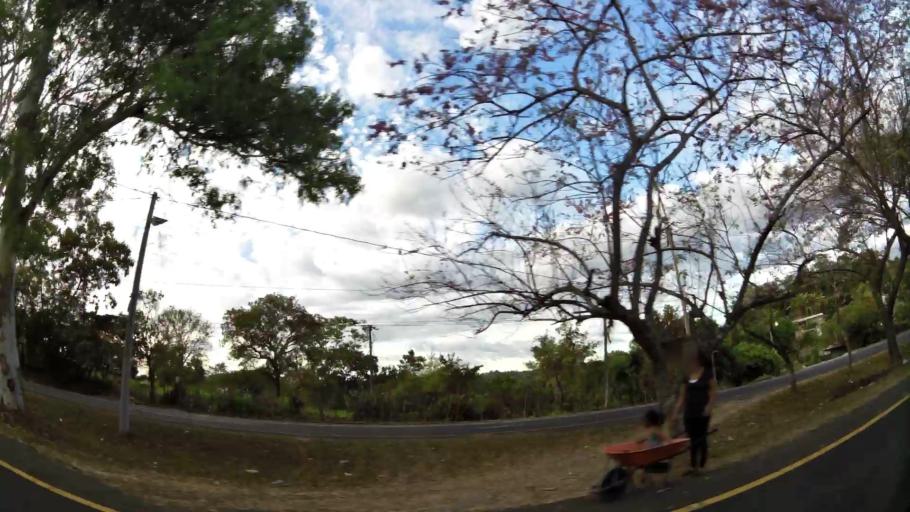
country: SV
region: San Vicente
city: San Sebastian
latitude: 13.7299
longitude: -88.8742
